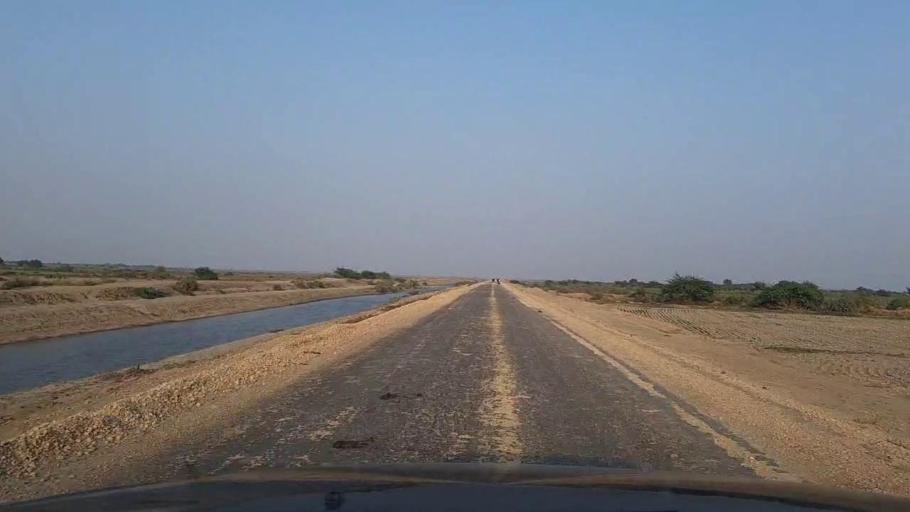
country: PK
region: Sindh
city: Mirpur Sakro
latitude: 24.4230
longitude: 67.7466
